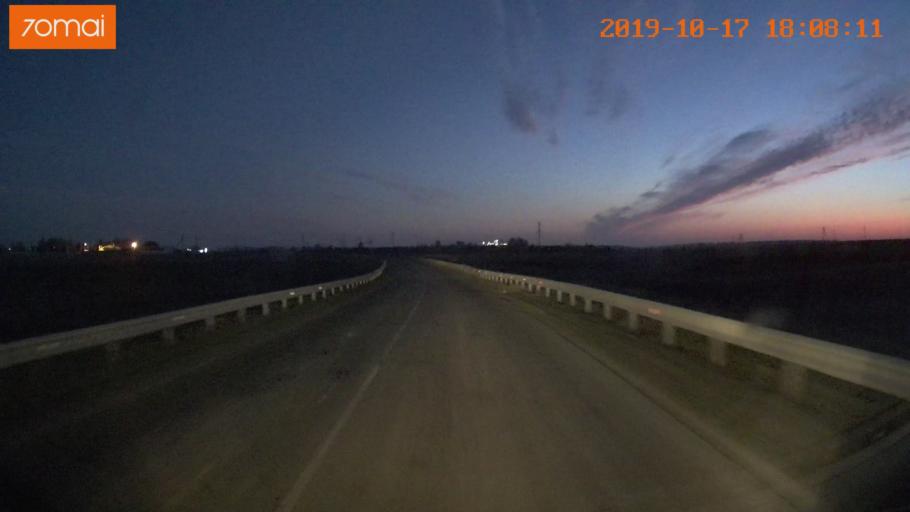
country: RU
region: Tula
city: Kurkino
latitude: 53.4367
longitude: 38.6437
